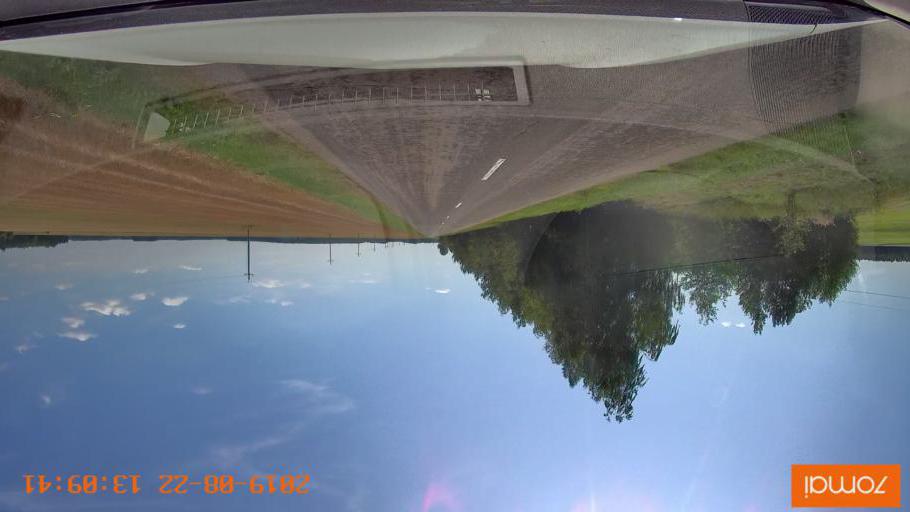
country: BY
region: Minsk
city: Prawdzinski
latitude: 53.3071
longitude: 27.8496
